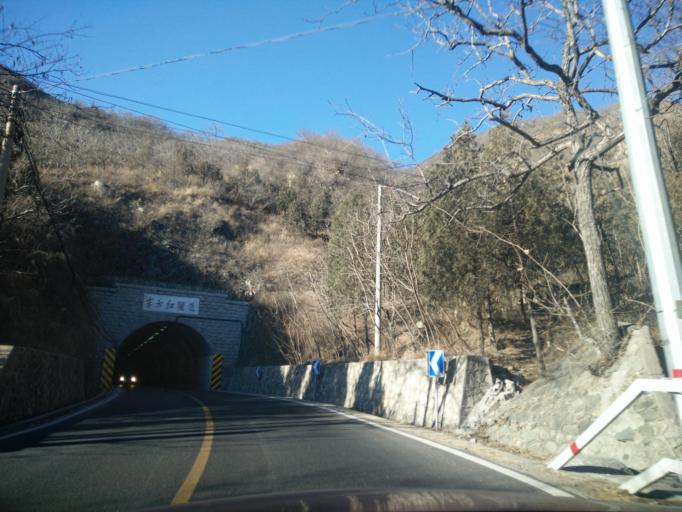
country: CN
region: Beijing
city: Wangping
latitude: 40.0066
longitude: 115.9664
